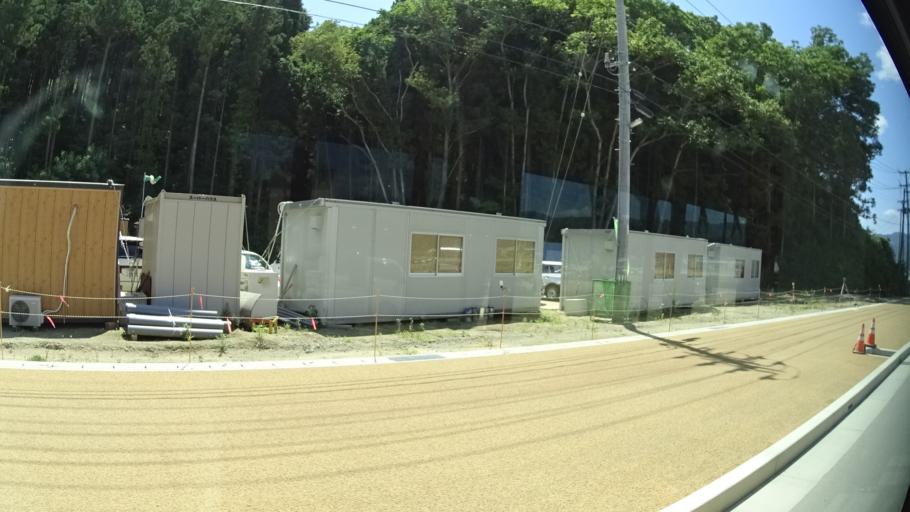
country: JP
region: Iwate
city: Ofunato
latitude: 39.0187
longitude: 141.6348
